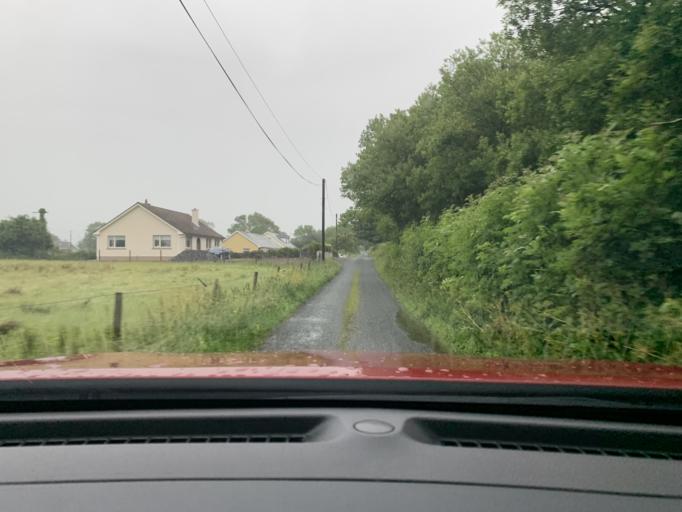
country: IE
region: Connaught
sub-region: Sligo
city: Sligo
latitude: 54.3195
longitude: -8.4527
